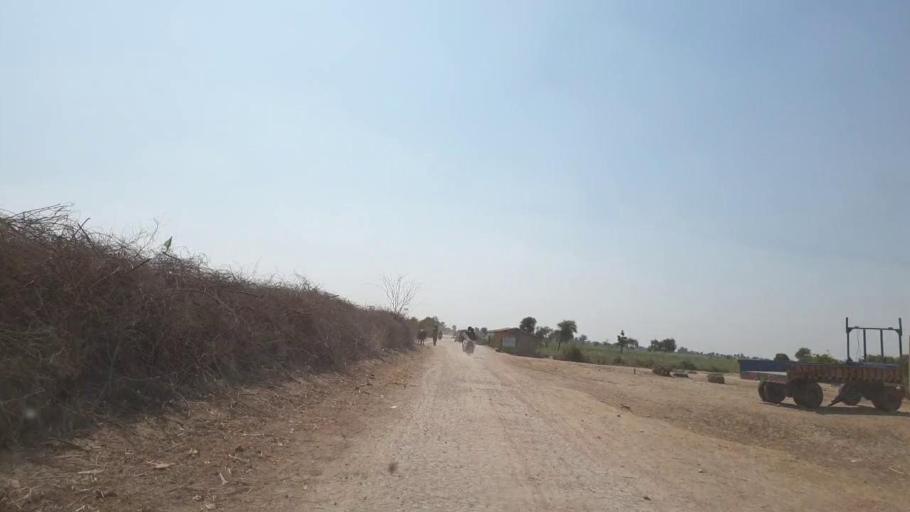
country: PK
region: Sindh
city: Mirpur Khas
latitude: 25.7461
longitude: 69.0843
